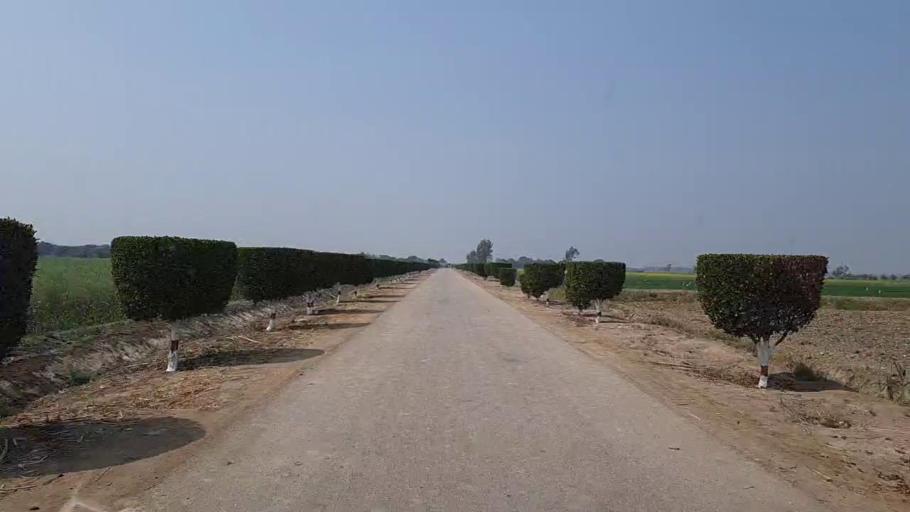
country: PK
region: Sindh
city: Mirwah Gorchani
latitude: 25.3357
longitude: 69.0012
